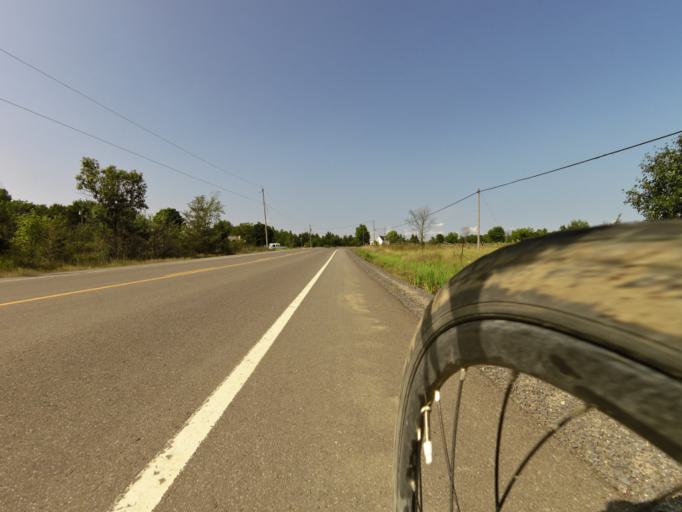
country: CA
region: Ontario
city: Skatepark
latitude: 44.2626
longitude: -76.7240
